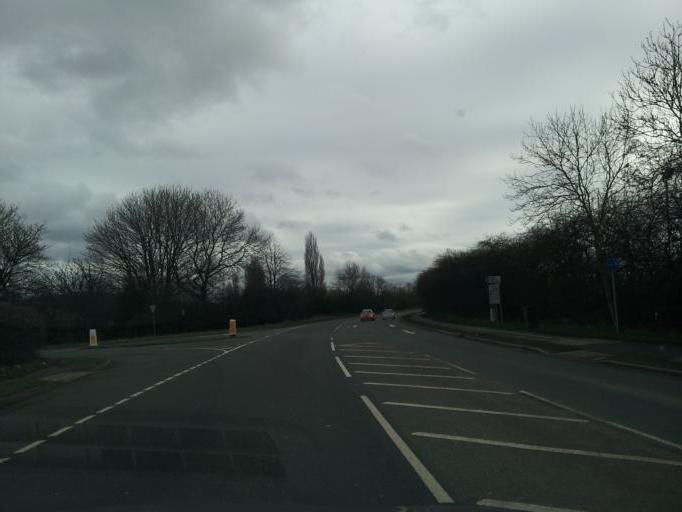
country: GB
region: England
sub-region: Staffordshire
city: Stafford
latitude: 52.8292
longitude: -2.1064
